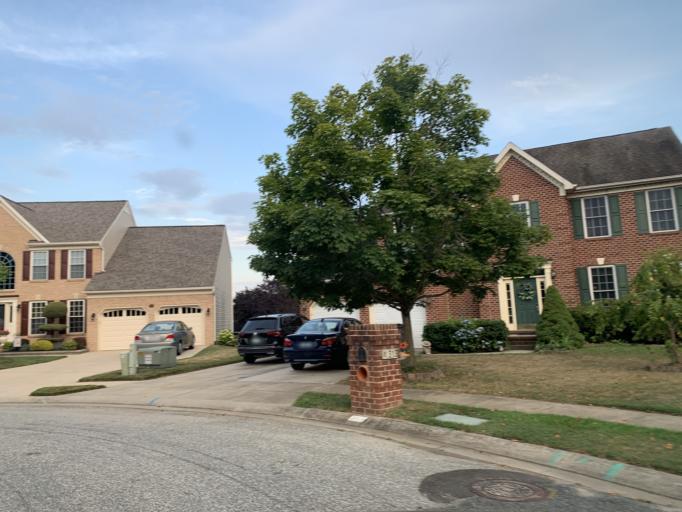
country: US
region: Maryland
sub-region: Harford County
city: Bel Air North
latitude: 39.5649
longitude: -76.3687
